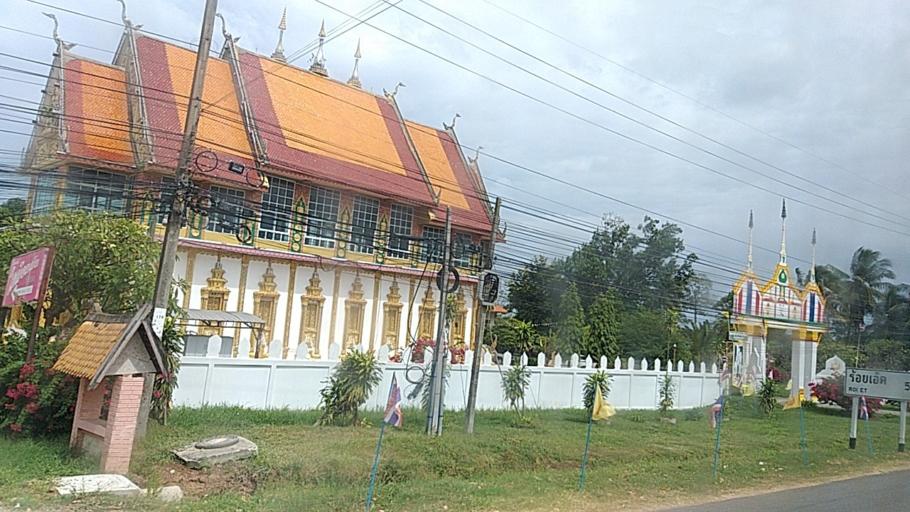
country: TH
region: Roi Et
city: Roi Et
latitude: 16.0670
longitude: 103.6106
